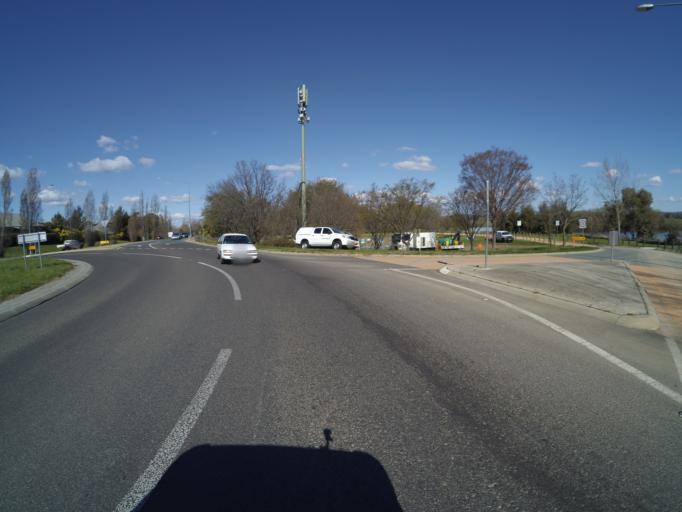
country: AU
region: Australian Capital Territory
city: Forrest
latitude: -35.3033
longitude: 149.1616
